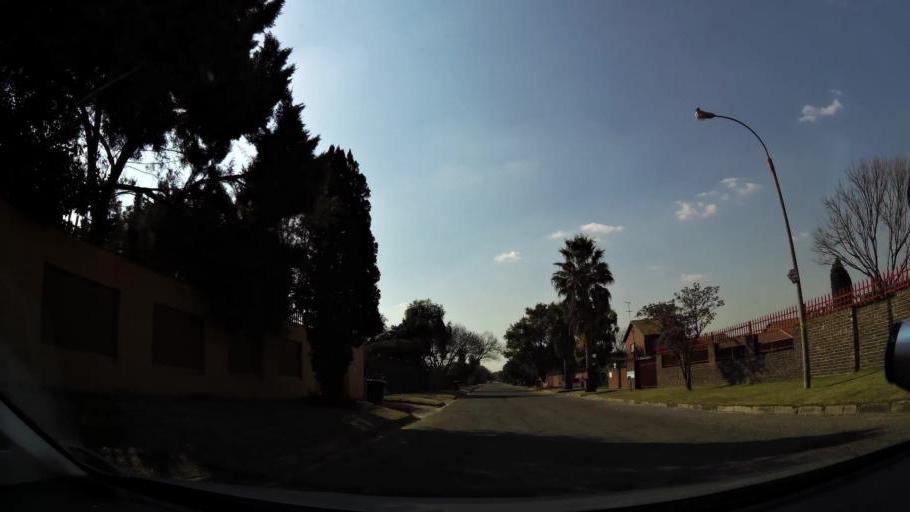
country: ZA
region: Gauteng
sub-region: City of Johannesburg Metropolitan Municipality
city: Modderfontein
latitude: -26.0952
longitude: 28.2153
